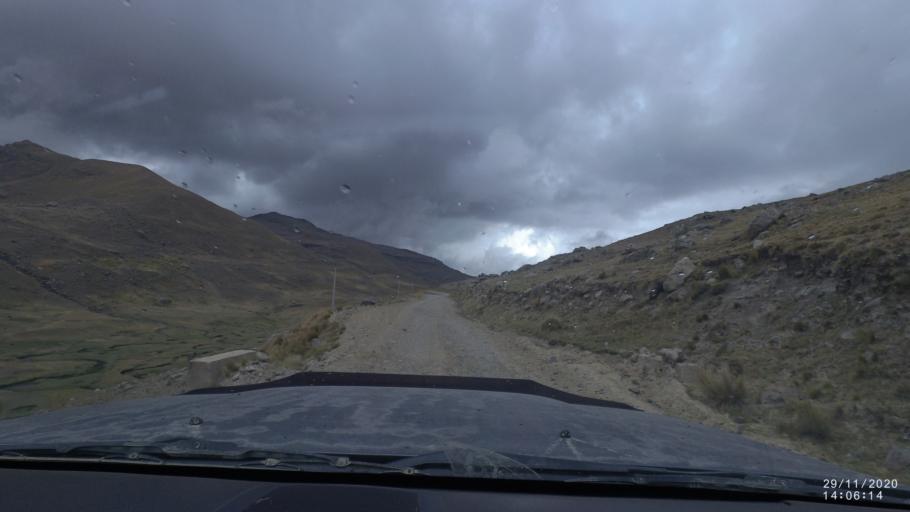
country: BO
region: Cochabamba
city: Sipe Sipe
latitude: -17.2123
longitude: -66.3778
